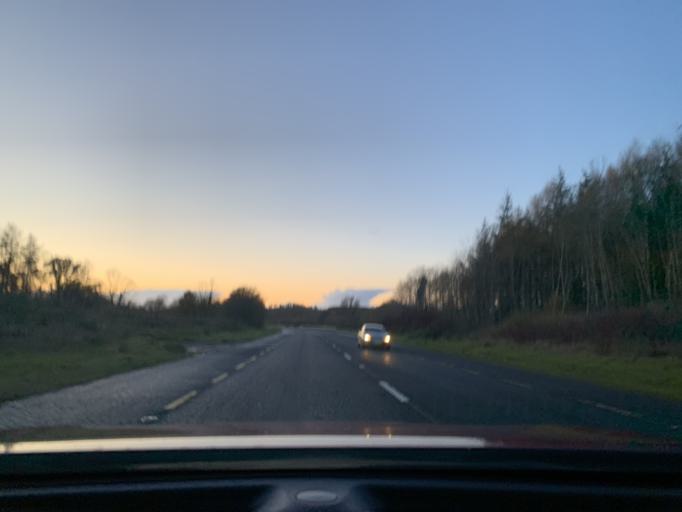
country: IE
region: Connaught
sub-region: County Leitrim
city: Carrick-on-Shannon
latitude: 53.9367
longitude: -8.0201
